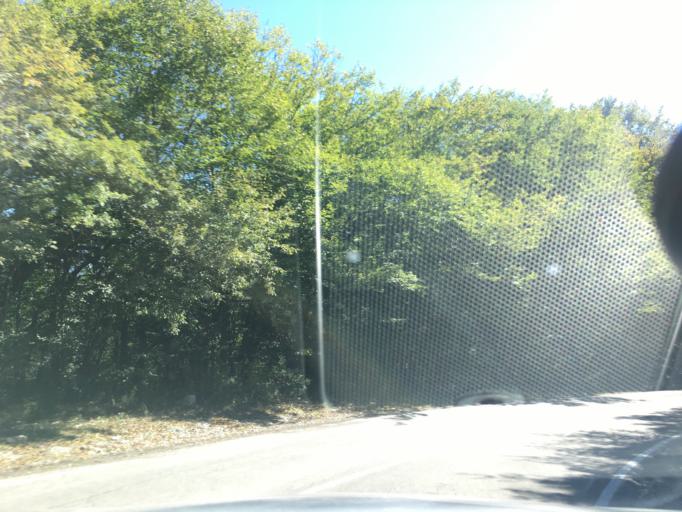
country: GE
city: Didi Lilo
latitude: 41.8771
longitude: 44.9093
